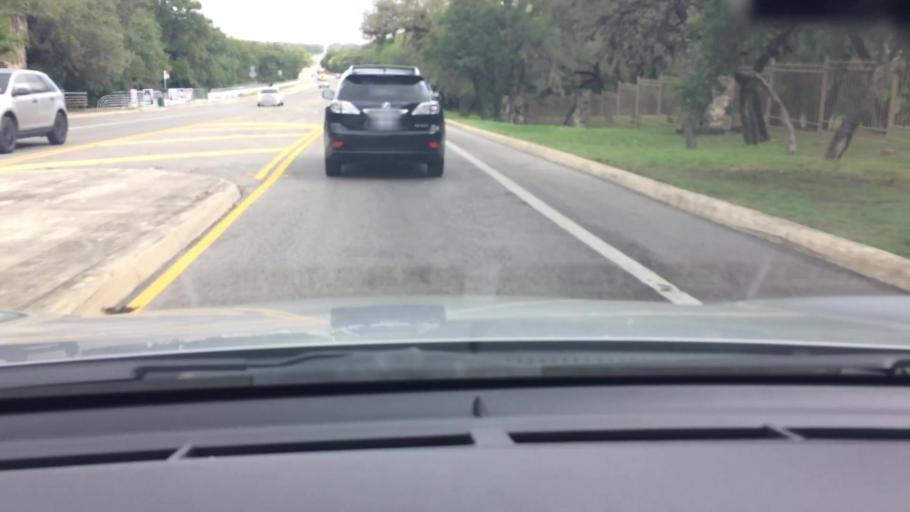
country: US
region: Texas
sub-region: Bexar County
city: Shavano Park
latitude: 29.5563
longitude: -98.5479
